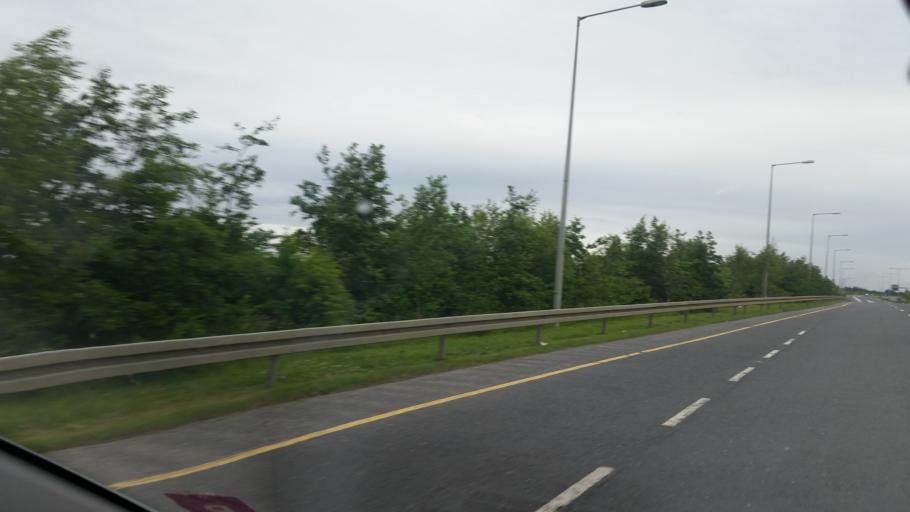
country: IE
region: Leinster
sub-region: Fingal County
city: Blanchardstown
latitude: 53.4324
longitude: -6.3438
